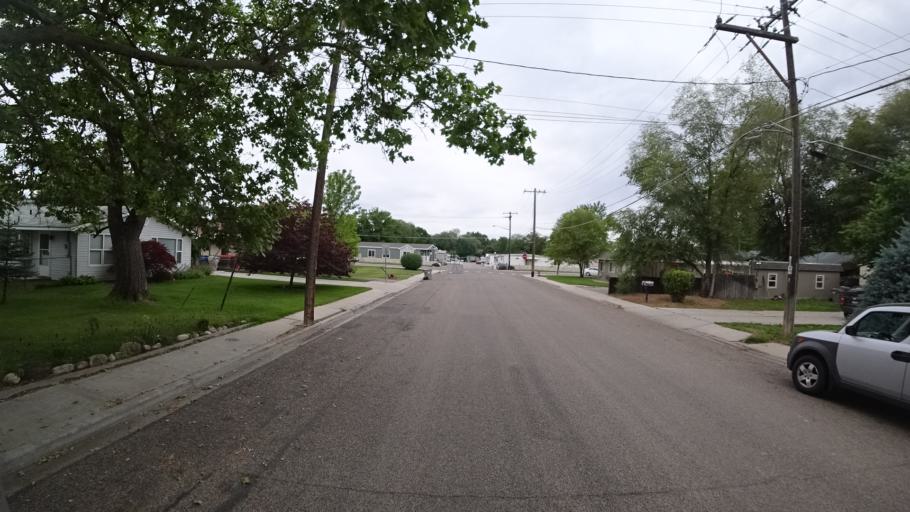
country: US
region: Idaho
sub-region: Ada County
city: Boise
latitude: 43.5808
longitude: -116.2229
